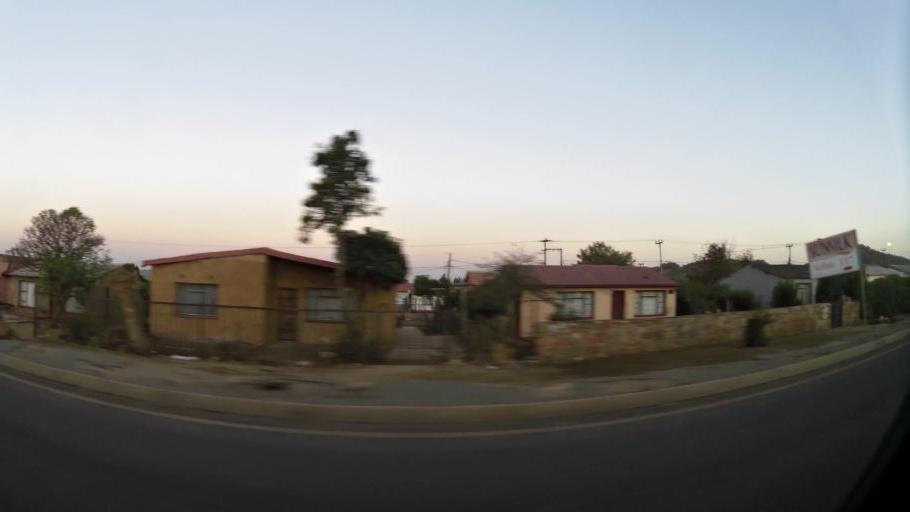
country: ZA
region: North-West
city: Ga-Rankuwa
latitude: -25.5964
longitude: 27.9778
